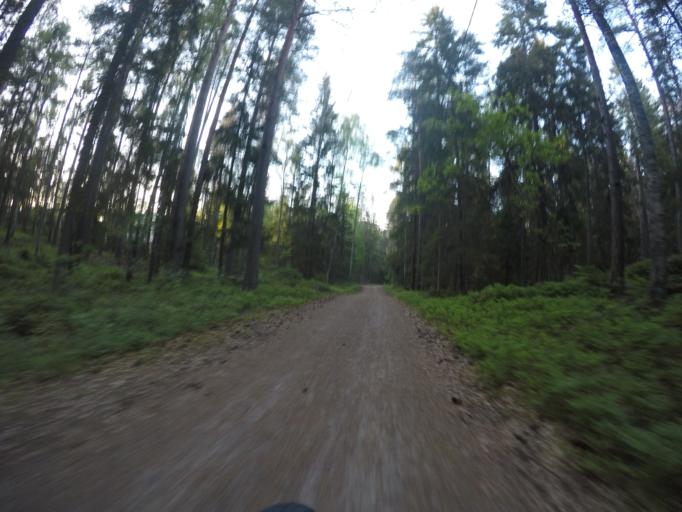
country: SE
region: Soedermanland
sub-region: Eskilstuna Kommun
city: Eskilstuna
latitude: 59.3407
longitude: 16.5111
